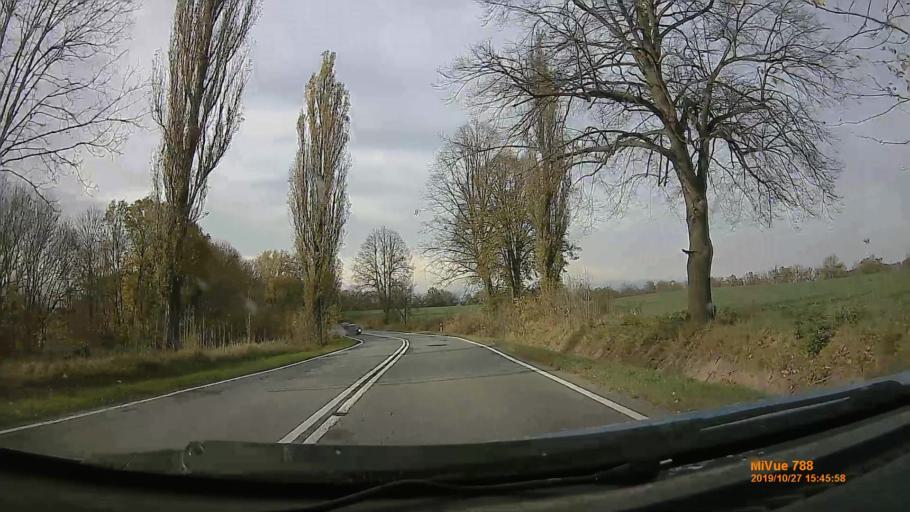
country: PL
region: Lower Silesian Voivodeship
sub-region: Powiat klodzki
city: Bozkow
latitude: 50.4784
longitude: 16.5902
